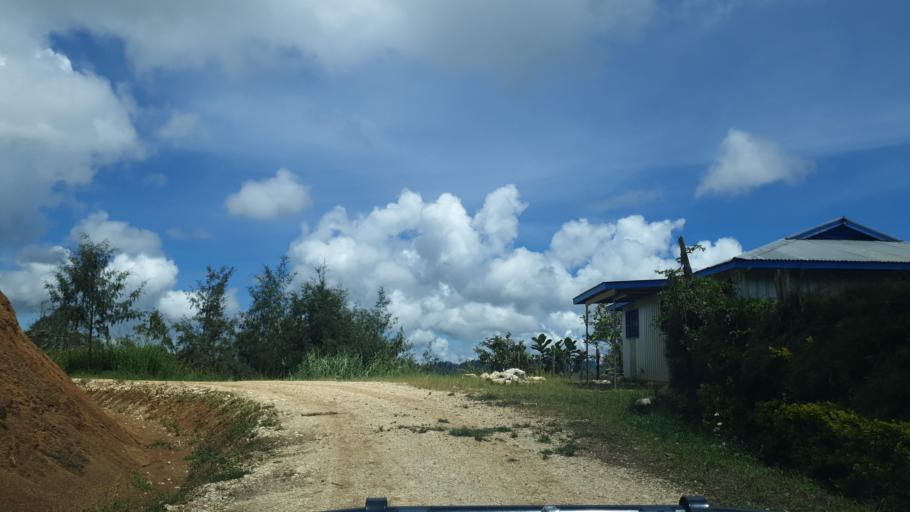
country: PG
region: Chimbu
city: Kundiawa
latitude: -6.2153
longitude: 145.1370
